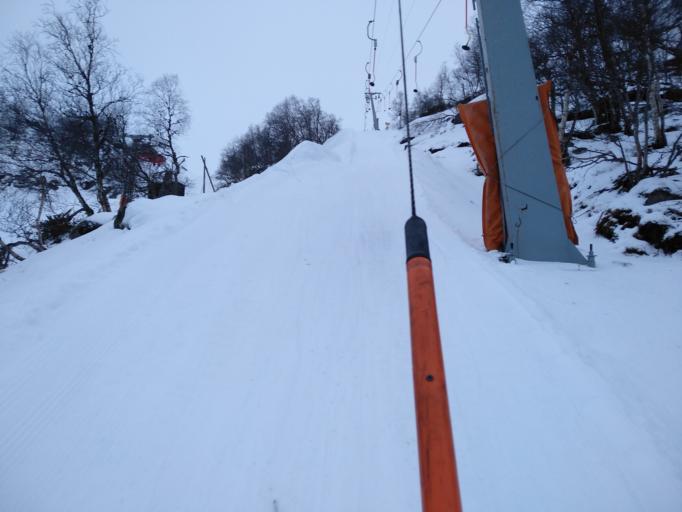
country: NO
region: Vest-Agder
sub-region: Sirdal
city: Tonstad
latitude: 59.0231
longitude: 6.9170
